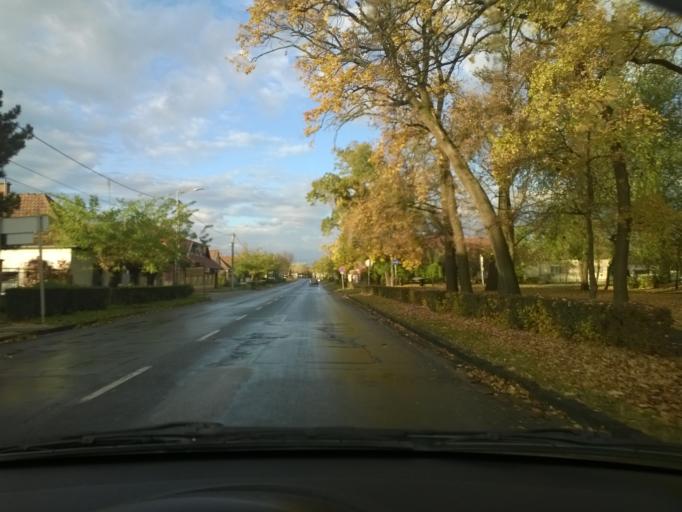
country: HU
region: Bacs-Kiskun
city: Kalocsa
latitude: 46.5357
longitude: 18.9855
